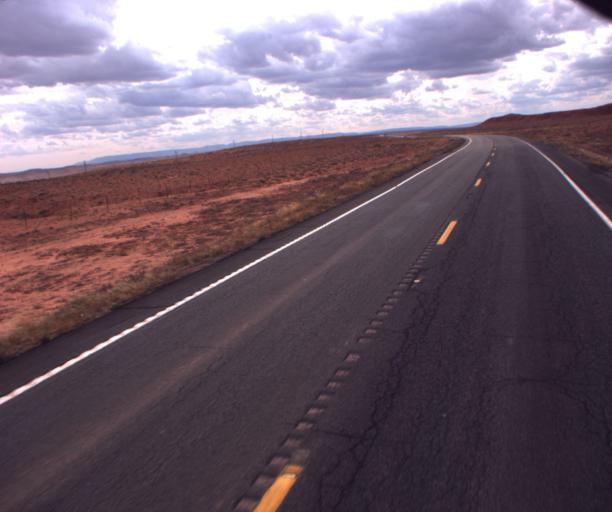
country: US
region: Arizona
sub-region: Navajo County
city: Kayenta
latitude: 36.9060
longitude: -109.7871
